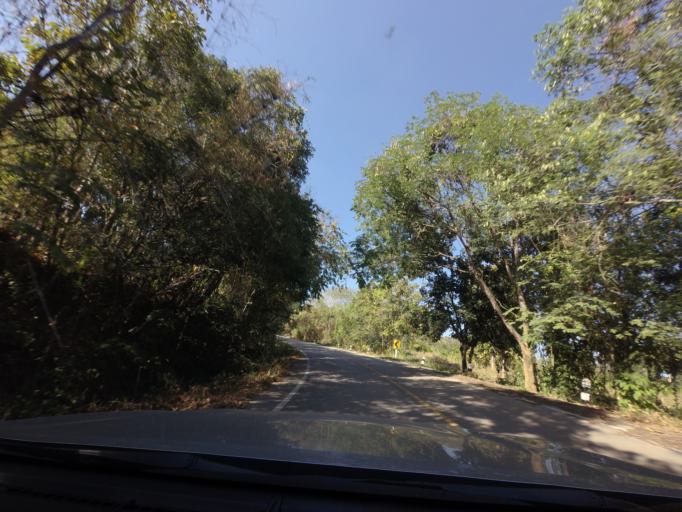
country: TH
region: Lampang
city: Chae Hom
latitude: 18.5445
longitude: 99.6379
